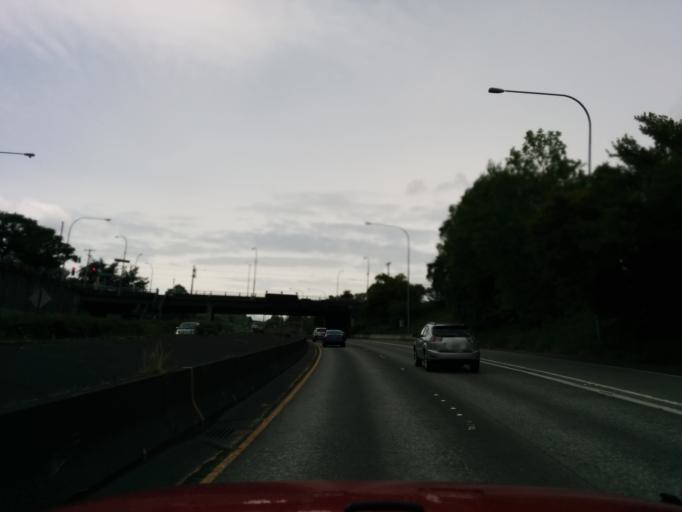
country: US
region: Washington
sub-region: King County
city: Seattle
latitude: 47.6445
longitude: -122.3028
